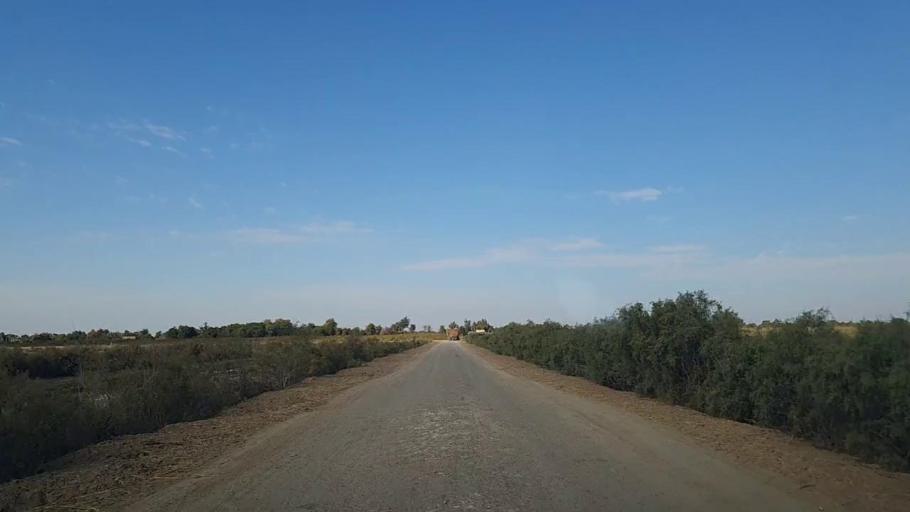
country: PK
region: Sindh
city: Khadro
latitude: 26.2998
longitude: 68.8202
